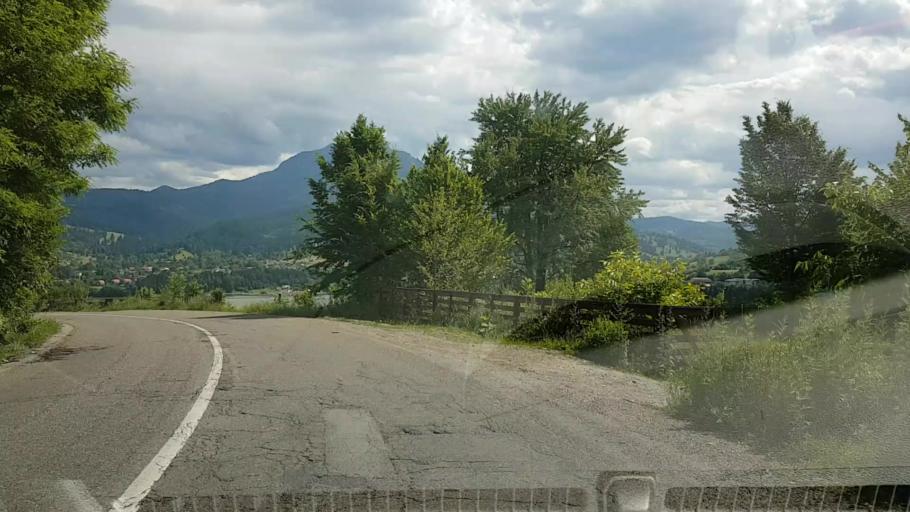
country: RO
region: Neamt
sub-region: Comuna Ceahlau
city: Ceahlau
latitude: 47.0604
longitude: 25.9684
